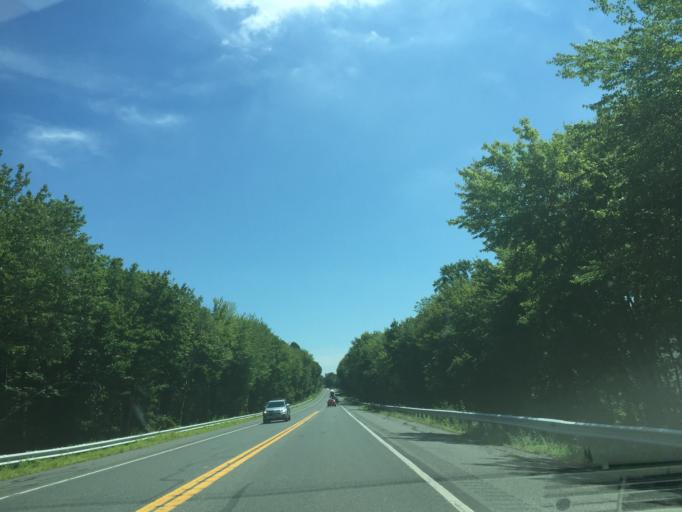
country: US
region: Maryland
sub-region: Harford County
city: Bel Air North
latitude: 39.5732
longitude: -76.3687
